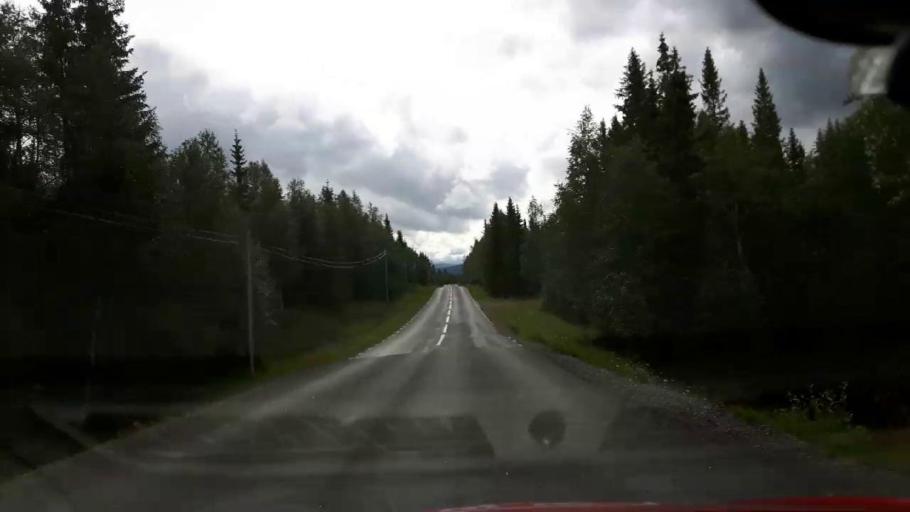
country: NO
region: Nord-Trondelag
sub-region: Lierne
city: Sandvika
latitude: 64.5223
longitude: 14.1638
